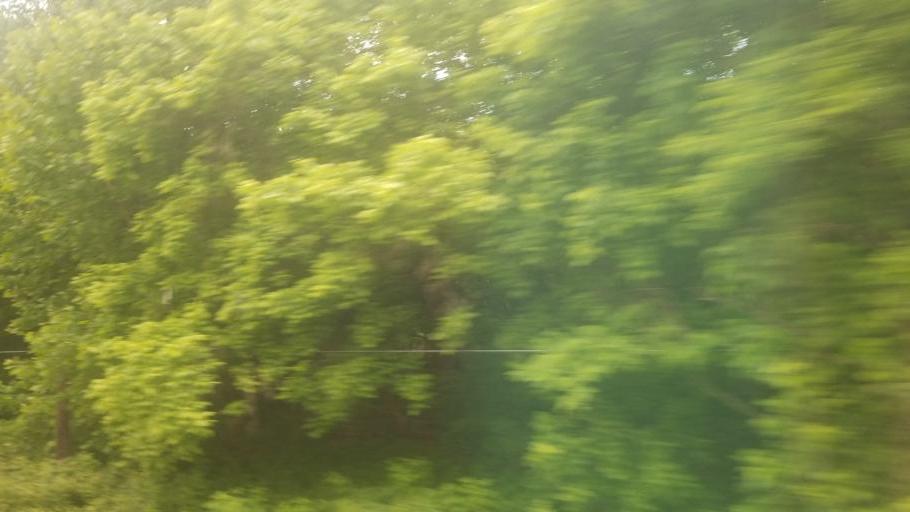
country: US
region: Maryland
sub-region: Frederick County
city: Brunswick
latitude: 39.3255
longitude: -77.6639
